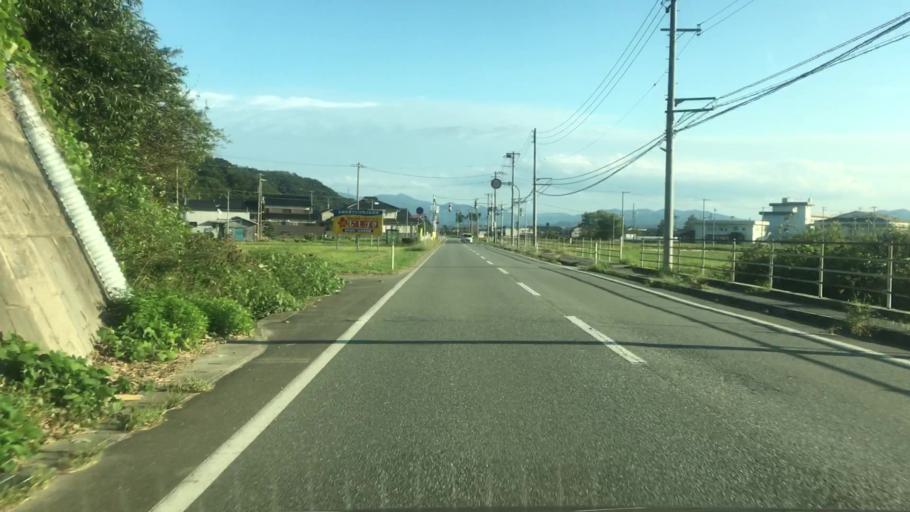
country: JP
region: Hyogo
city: Toyooka
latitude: 35.5663
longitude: 134.8195
